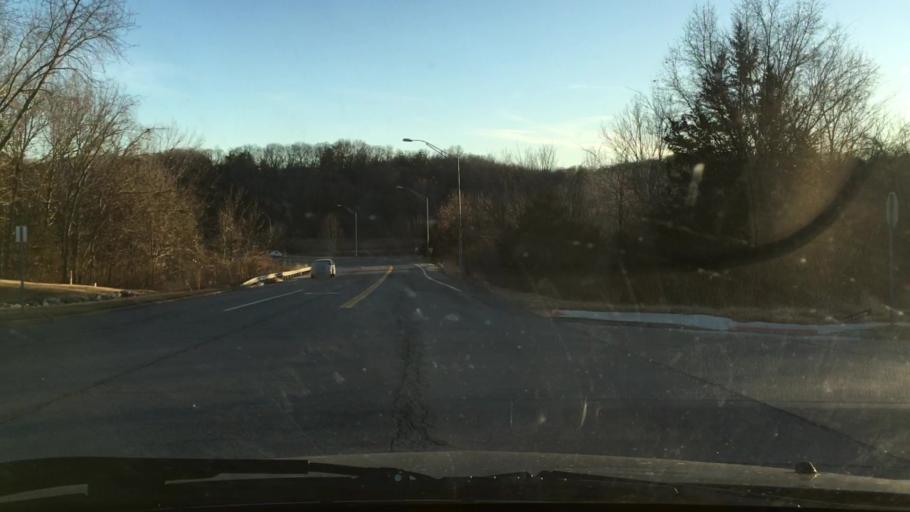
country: US
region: Missouri
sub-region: Boone County
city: Columbia
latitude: 38.9243
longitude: -92.3652
